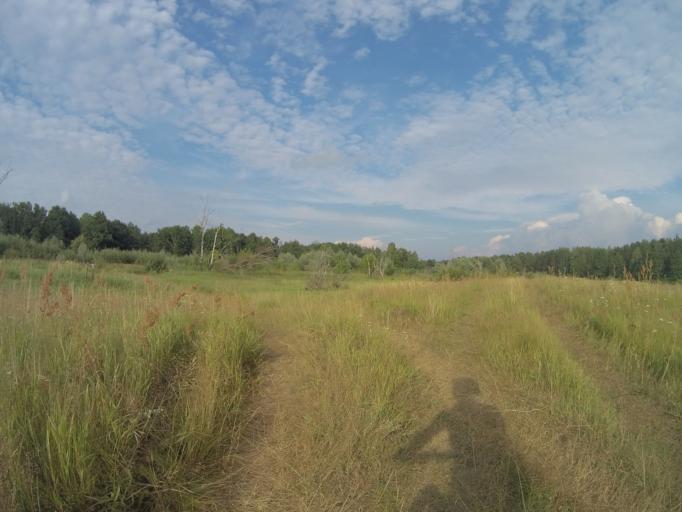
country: RU
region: Vladimir
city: Vorsha
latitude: 56.0076
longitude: 40.0751
